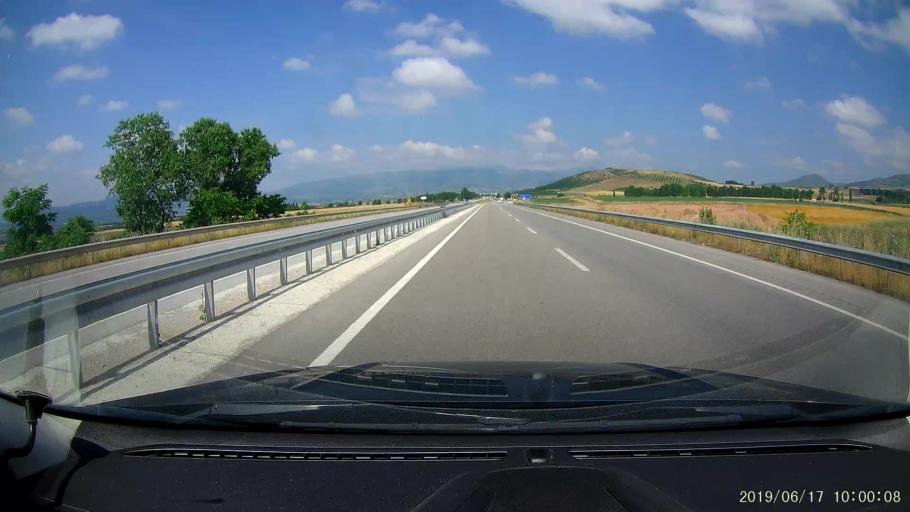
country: TR
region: Amasya
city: Alicik
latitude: 40.8664
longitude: 35.2959
